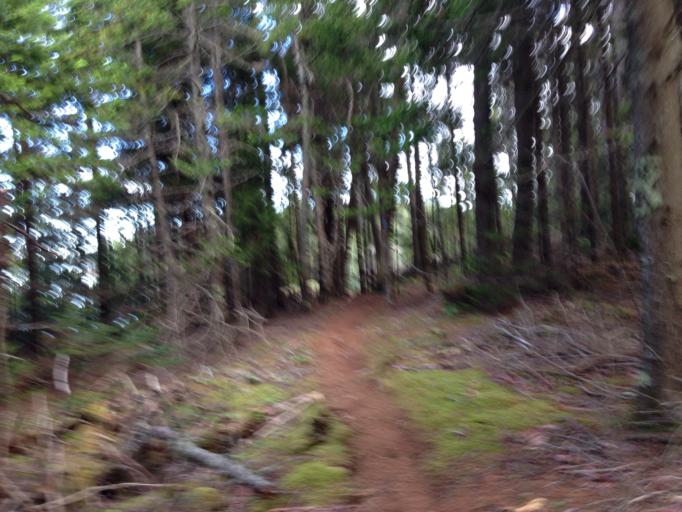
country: US
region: Maine
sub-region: Hancock County
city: Gouldsboro
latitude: 44.3820
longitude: -68.0722
